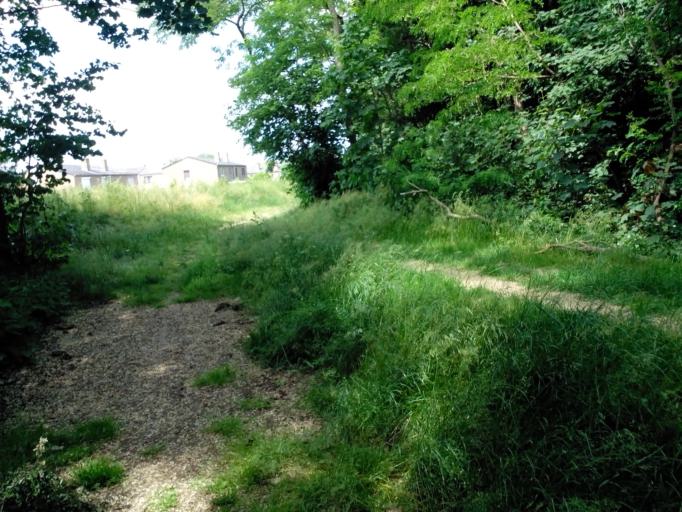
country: BE
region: Flanders
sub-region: Provincie Vlaams-Brabant
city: Leuven
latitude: 50.9058
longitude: 4.7216
